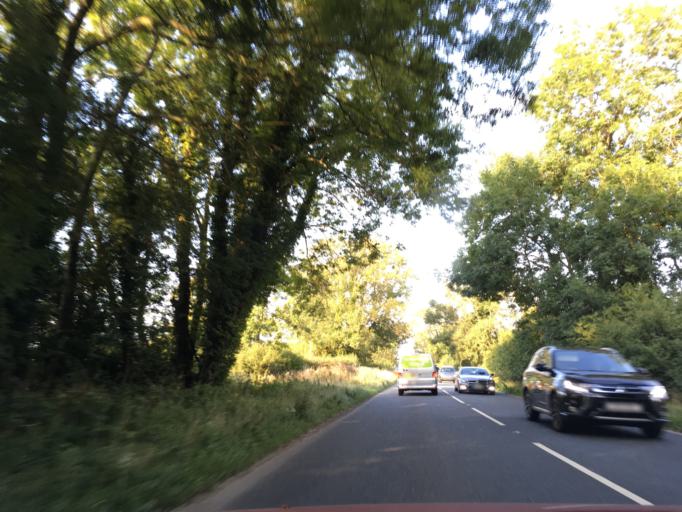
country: GB
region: England
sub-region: Gloucestershire
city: Stow on the Wold
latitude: 51.9054
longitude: -1.7418
